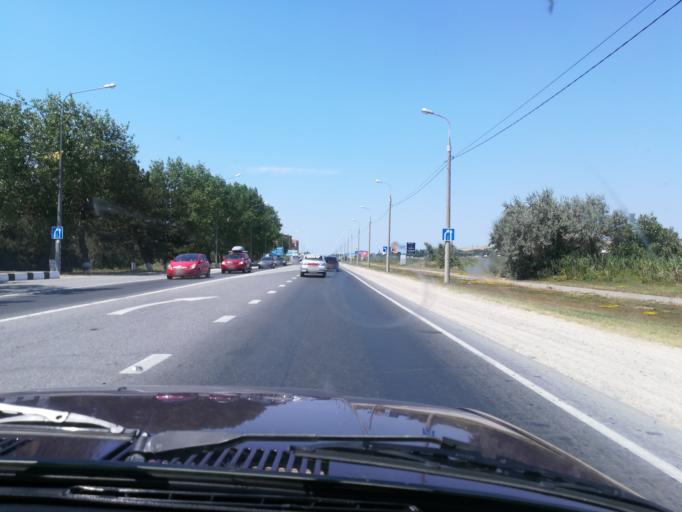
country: RU
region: Krasnodarskiy
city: Anapa
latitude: 44.9334
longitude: 37.3215
